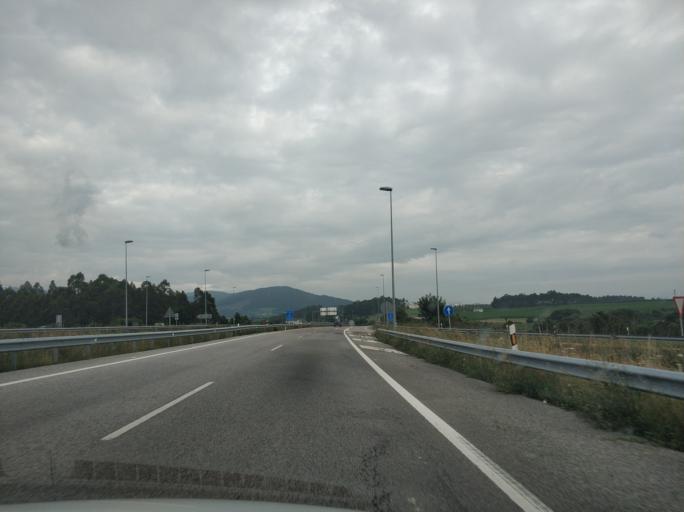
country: ES
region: Asturias
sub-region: Province of Asturias
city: Navia
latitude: 43.5326
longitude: -6.6941
